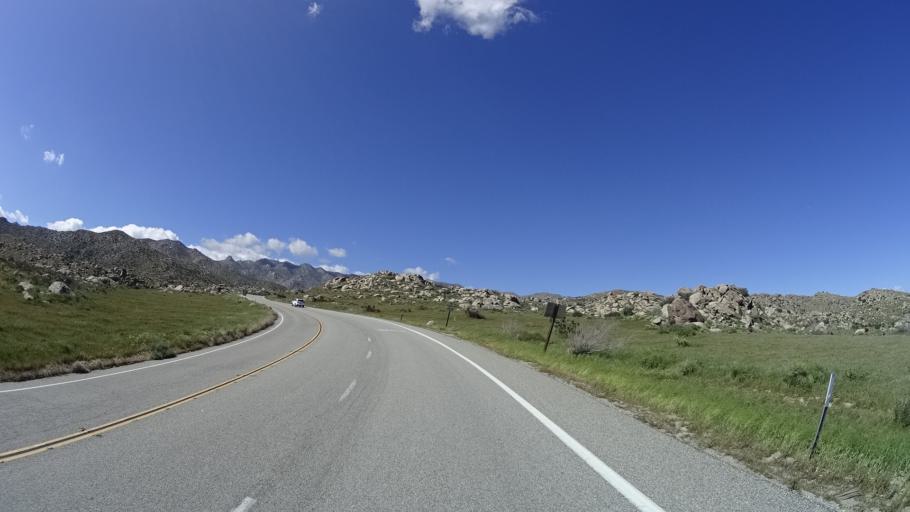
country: US
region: California
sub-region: San Diego County
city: Borrego Springs
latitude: 33.2166
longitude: -116.4509
